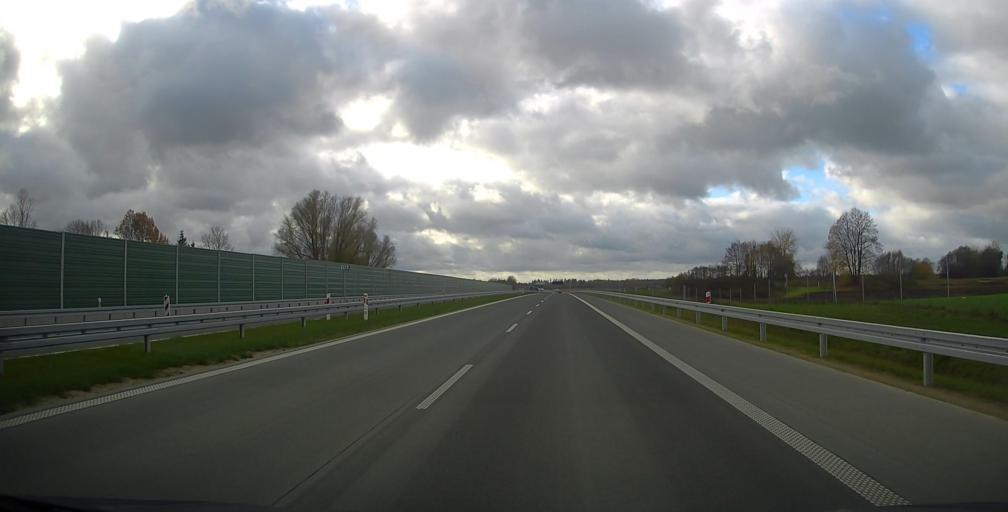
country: PL
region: Podlasie
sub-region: Powiat suwalski
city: Raczki
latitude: 53.9105
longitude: 22.7174
